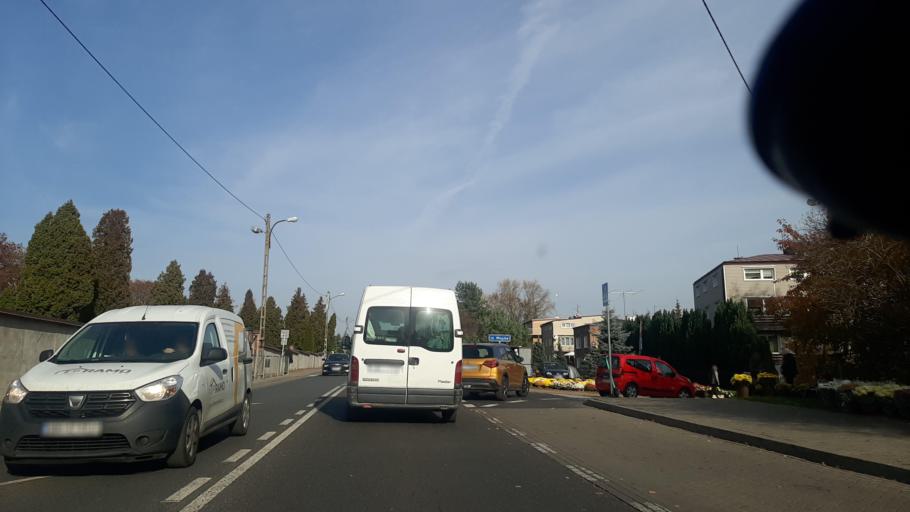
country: PL
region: Lublin Voivodeship
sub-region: Powiat lubelski
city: Lublin
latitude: 51.2633
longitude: 22.5809
